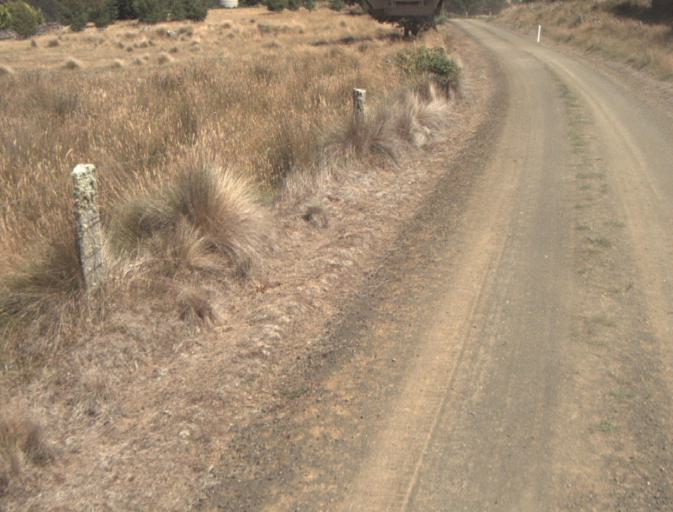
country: AU
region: Tasmania
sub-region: Dorset
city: Scottsdale
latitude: -41.3496
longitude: 147.4515
